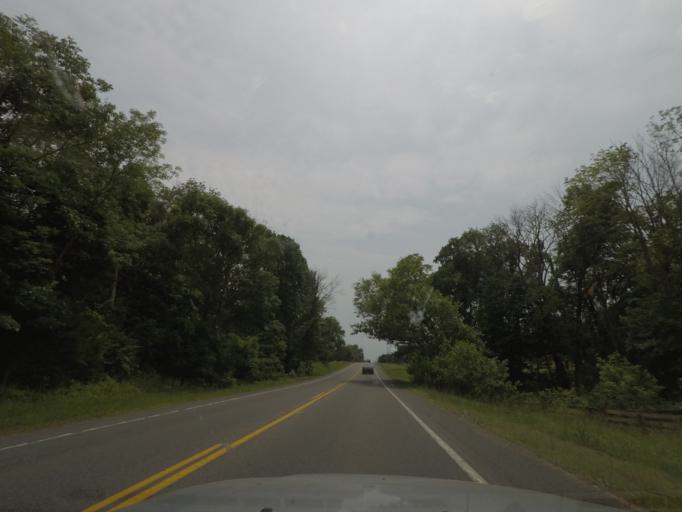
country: US
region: Virginia
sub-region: Prince William County
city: Bull Run Mountain Estates
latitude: 38.9402
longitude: -77.6237
